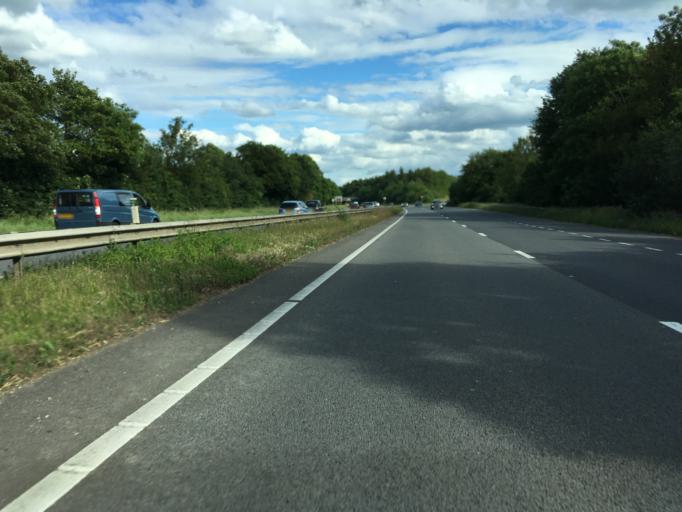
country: GB
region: England
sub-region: Oxfordshire
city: Wheatley
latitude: 51.7533
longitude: -1.1417
